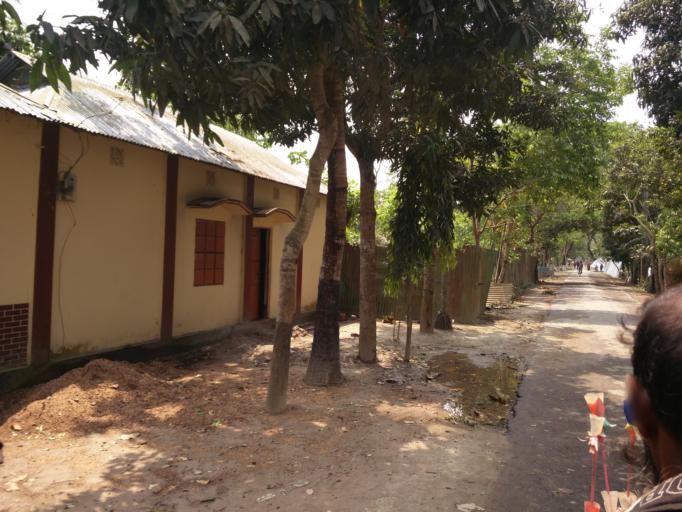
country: BD
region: Dhaka
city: Sherpur
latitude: 24.9577
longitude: 90.1713
